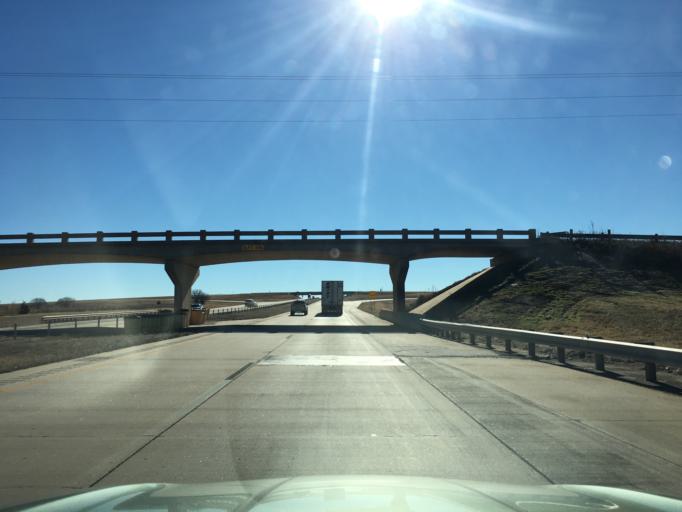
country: US
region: Oklahoma
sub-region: Noble County
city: Perry
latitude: 36.4065
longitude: -97.3272
